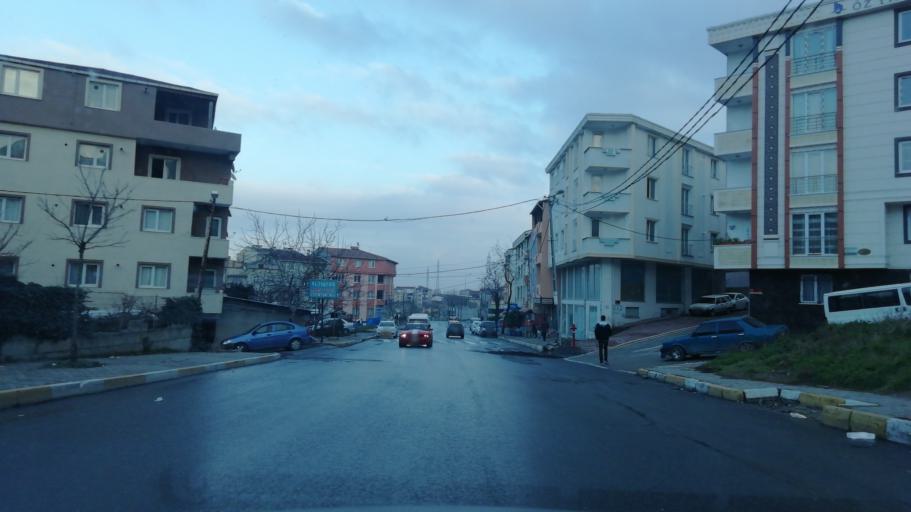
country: TR
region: Istanbul
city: Esenyurt
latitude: 41.0291
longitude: 28.6982
